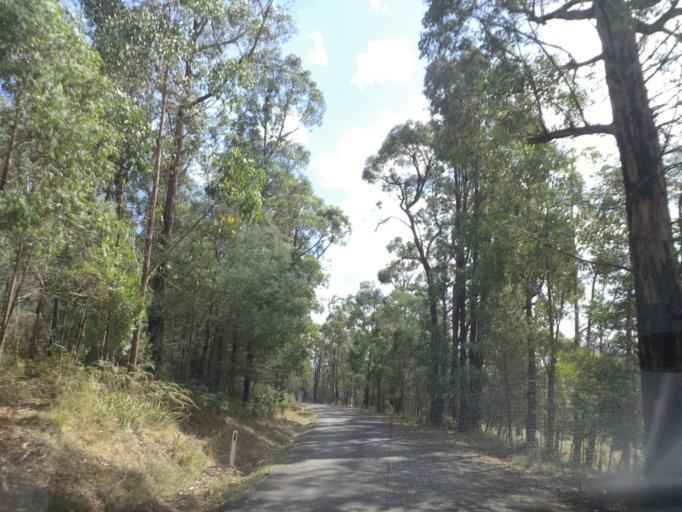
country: AU
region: Victoria
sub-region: Murrindindi
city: Alexandra
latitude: -37.4481
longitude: 145.7496
